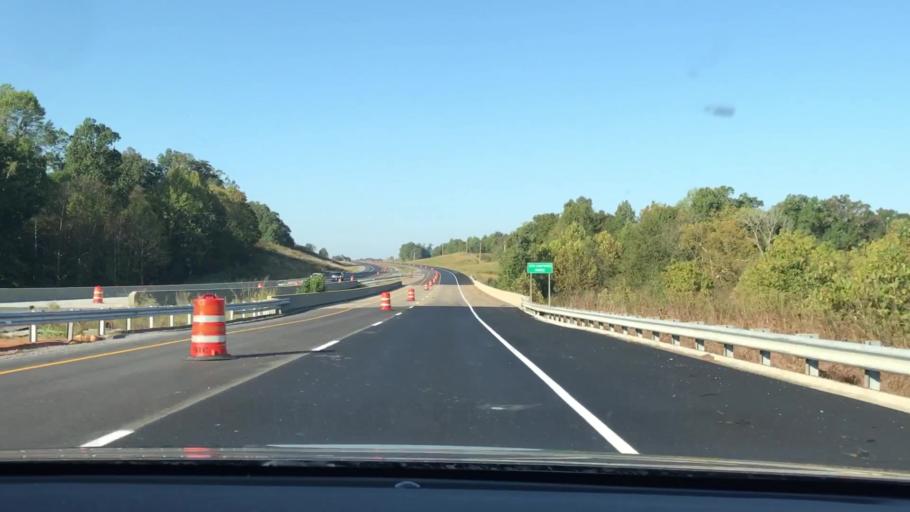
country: US
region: Kentucky
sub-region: Trigg County
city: Cadiz
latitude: 36.8422
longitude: -87.8317
